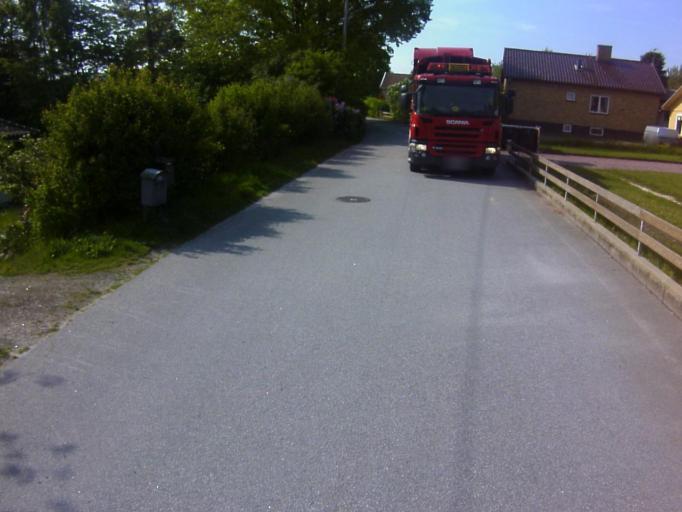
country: SE
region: Blekinge
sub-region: Karlshamns Kommun
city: Morrum
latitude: 56.0502
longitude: 14.7534
